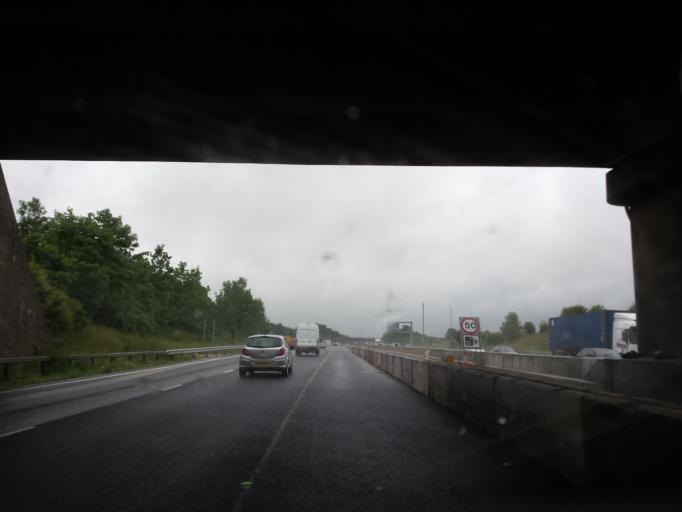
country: GB
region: England
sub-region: Derbyshire
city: Barlborough
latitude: 53.2861
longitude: -1.2960
